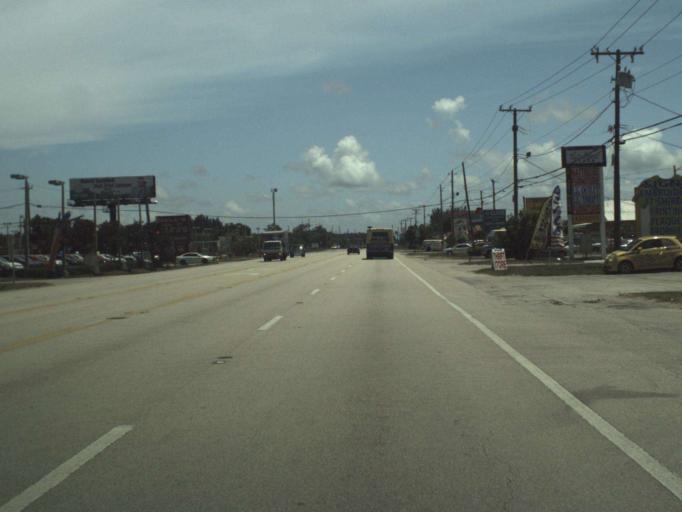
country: US
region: Florida
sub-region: Saint Lucie County
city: White City
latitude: 27.4011
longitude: -80.3259
